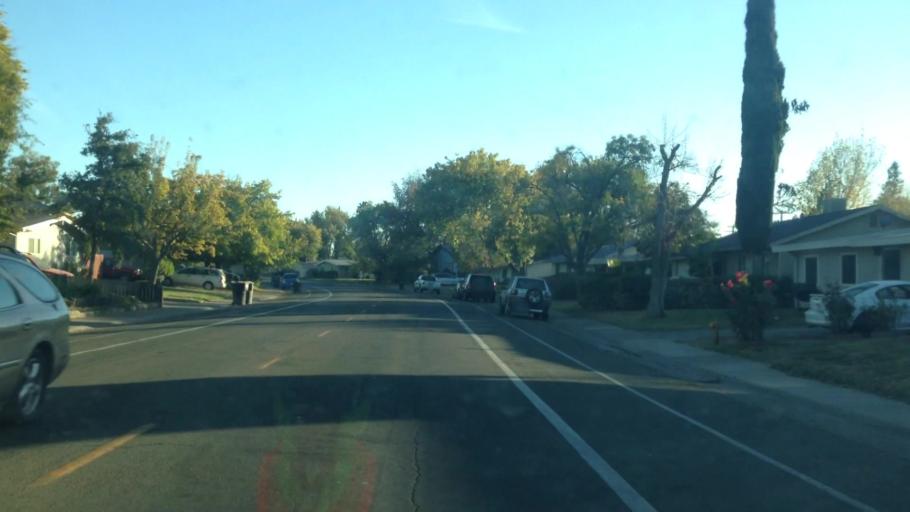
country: US
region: California
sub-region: Sacramento County
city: North Highlands
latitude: 38.6892
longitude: -121.3697
